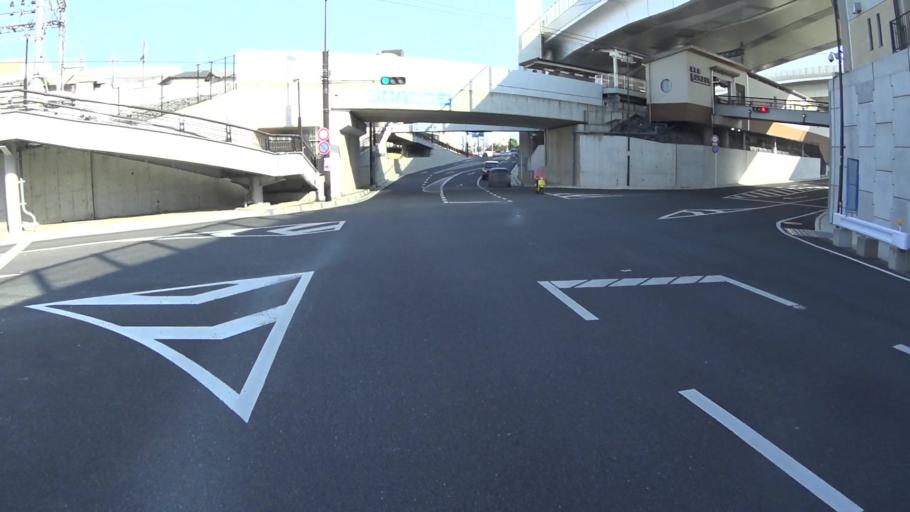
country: JP
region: Kyoto
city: Yawata
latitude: 34.9140
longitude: 135.6881
